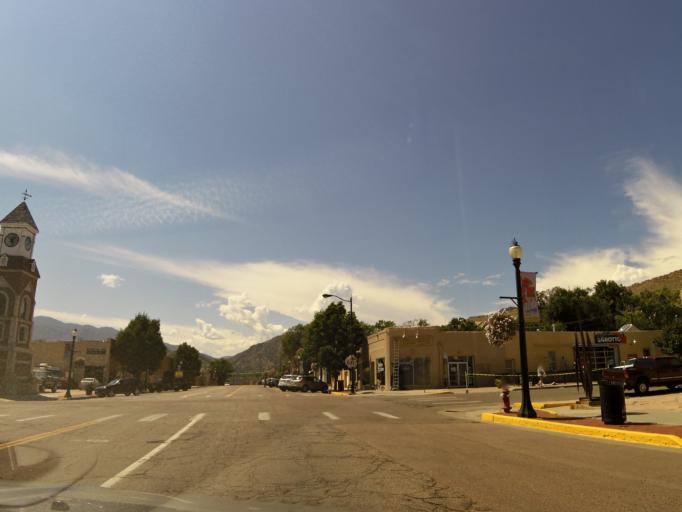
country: US
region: Colorado
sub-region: Fremont County
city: Canon City
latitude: 38.4395
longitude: -105.2431
